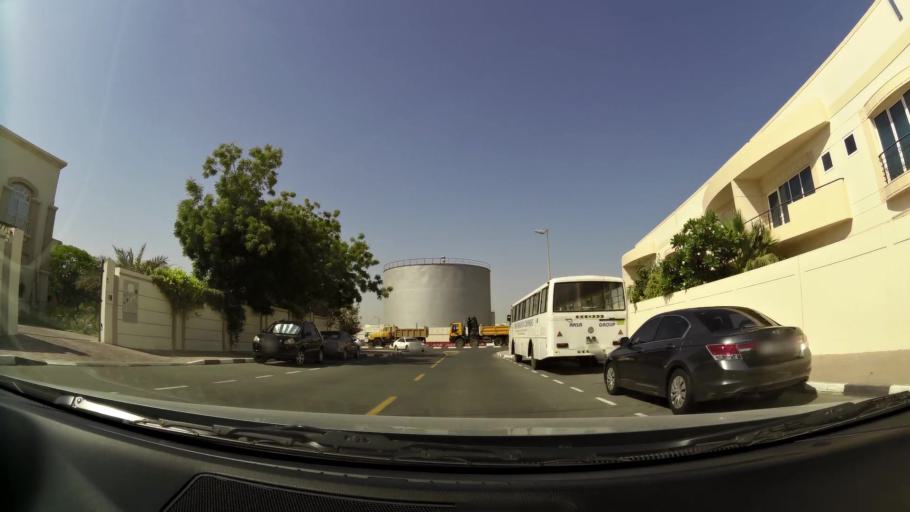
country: AE
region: Ash Shariqah
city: Sharjah
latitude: 25.2469
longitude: 55.2800
